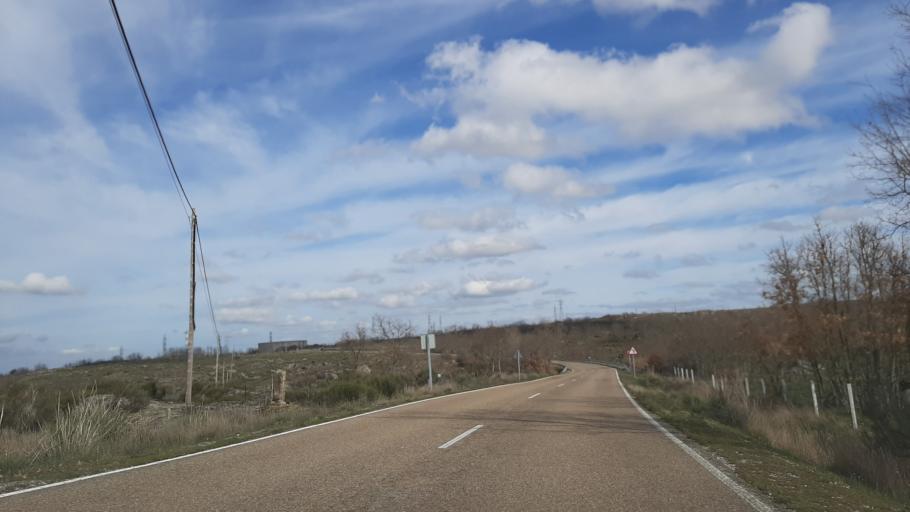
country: ES
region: Castille and Leon
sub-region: Provincia de Salamanca
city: Villarino de los Aires
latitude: 41.2471
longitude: -6.4988
